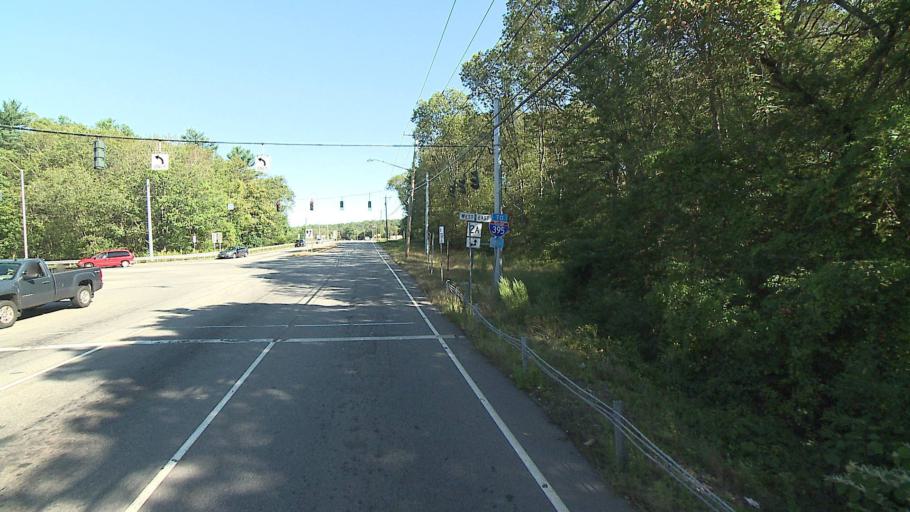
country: US
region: Connecticut
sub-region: New London County
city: Norwich
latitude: 41.4822
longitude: -72.0657
